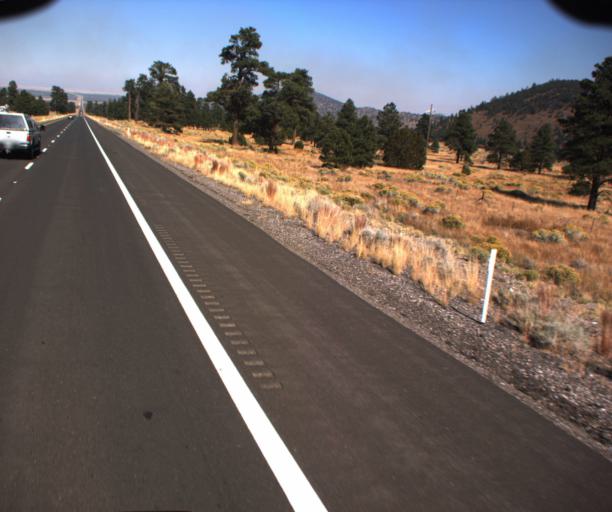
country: US
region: Arizona
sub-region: Coconino County
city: Flagstaff
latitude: 35.3844
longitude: -111.5800
